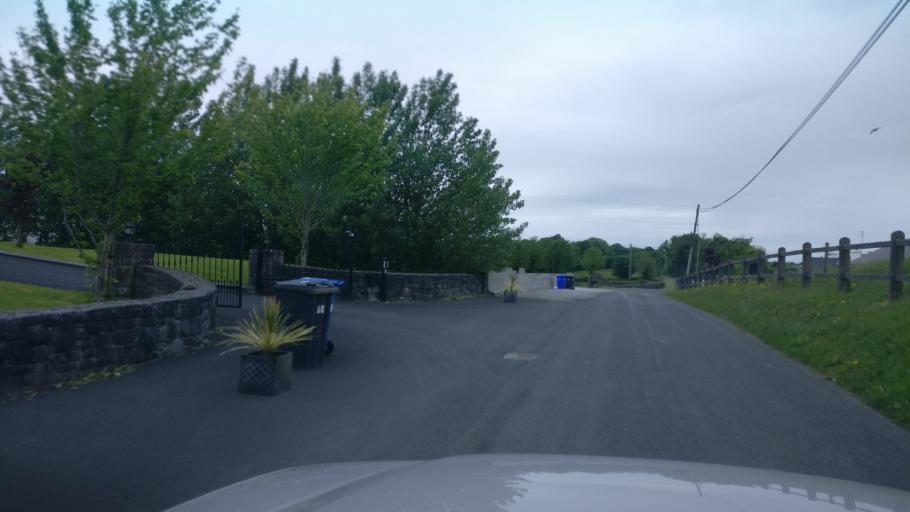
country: IE
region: Connaught
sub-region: County Galway
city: Loughrea
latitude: 53.1125
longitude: -8.4118
